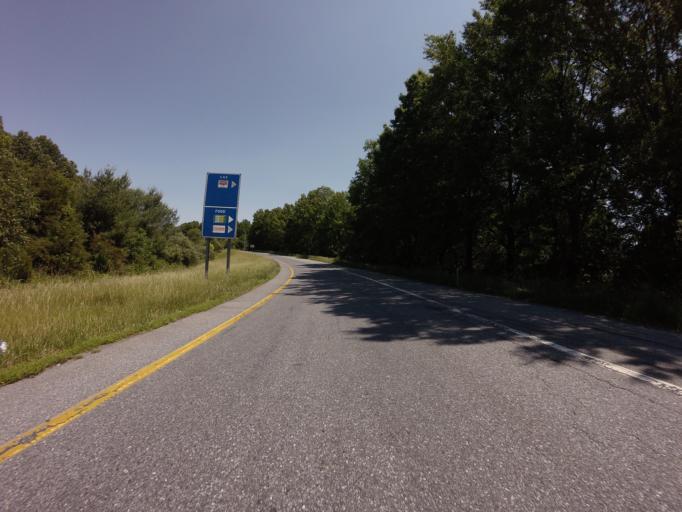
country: US
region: Maryland
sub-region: Carroll County
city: Sykesville
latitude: 39.3254
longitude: -77.0192
